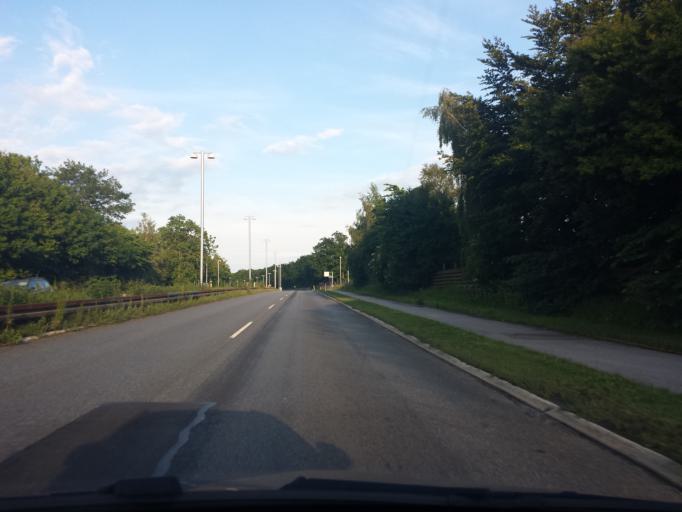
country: DK
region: Capital Region
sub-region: Ballerup Kommune
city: Ballerup
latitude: 55.7390
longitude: 12.3446
